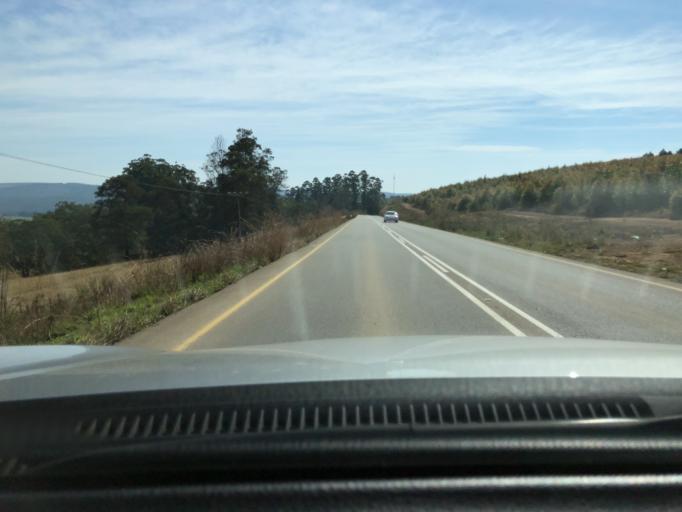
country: ZA
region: KwaZulu-Natal
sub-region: Sisonke District Municipality
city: Ixopo
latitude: -30.1759
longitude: 30.0605
